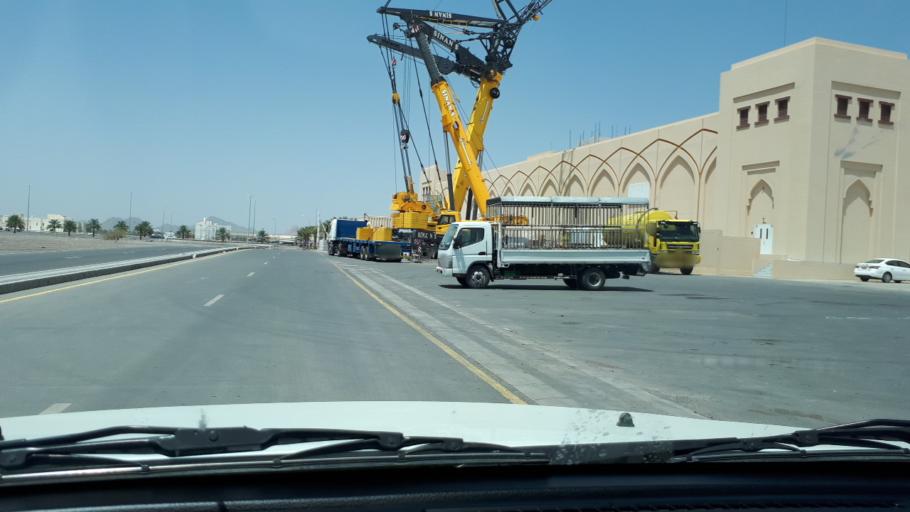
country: OM
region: Muhafazat ad Dakhiliyah
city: Nizwa
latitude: 22.8706
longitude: 57.5391
